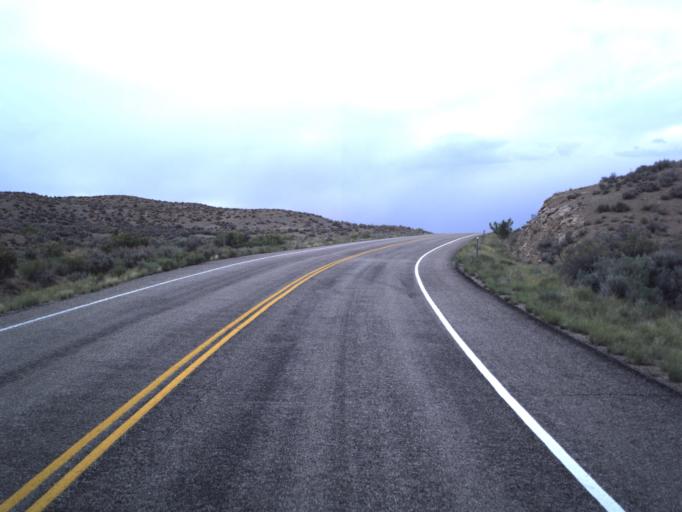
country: US
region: Colorado
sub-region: Rio Blanco County
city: Rangely
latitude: 40.0049
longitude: -109.1694
